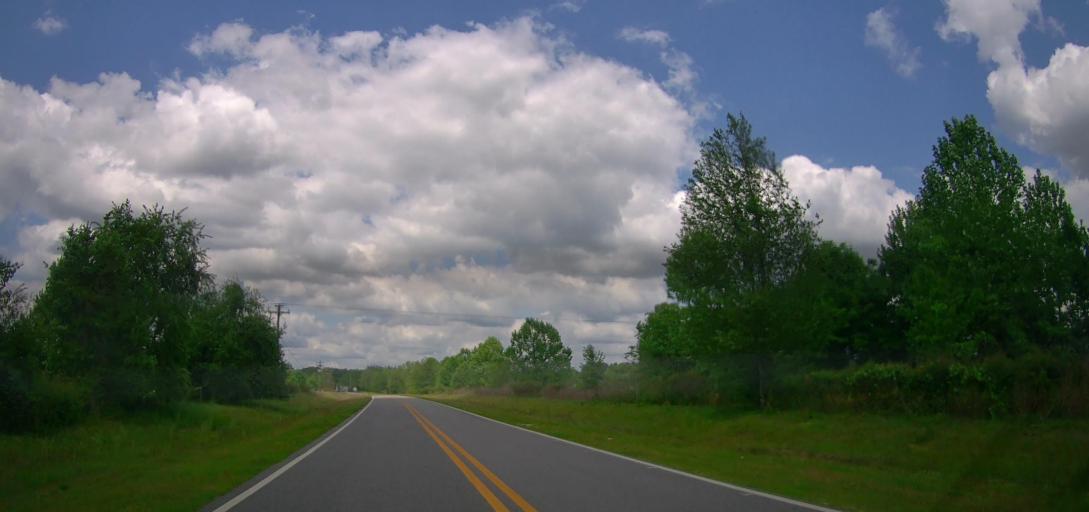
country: US
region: Georgia
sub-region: Laurens County
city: Dublin
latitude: 32.5960
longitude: -82.9304
